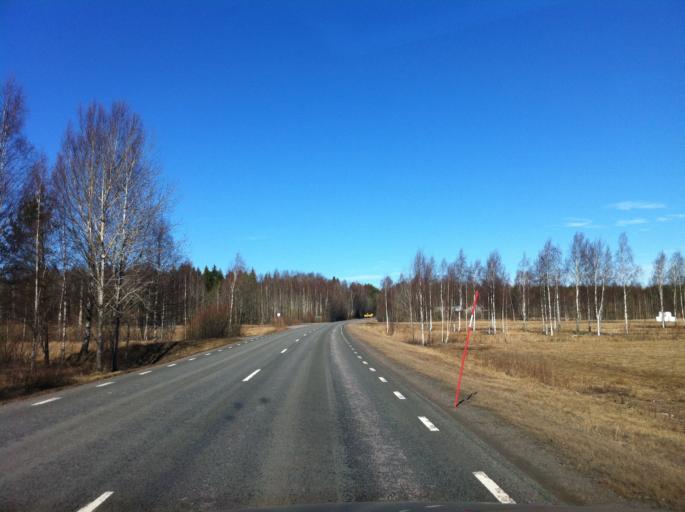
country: SE
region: Vaestra Goetaland
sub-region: Toreboda Kommun
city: Toereboda
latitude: 58.7863
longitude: 14.0845
